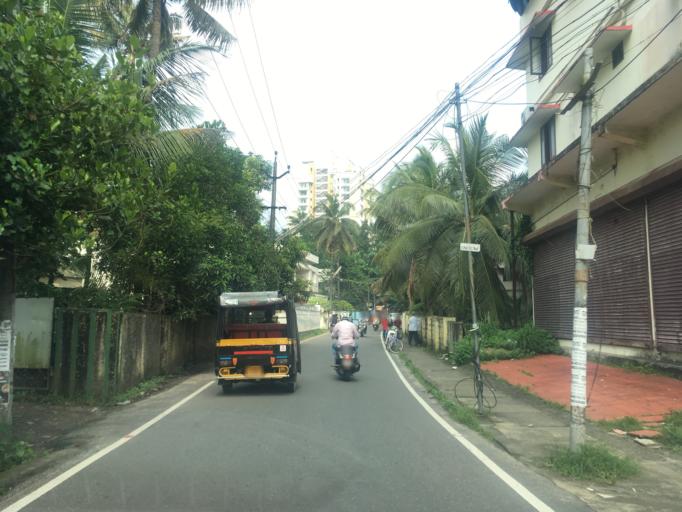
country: IN
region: Kerala
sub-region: Ernakulam
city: Elur
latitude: 10.0331
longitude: 76.3092
